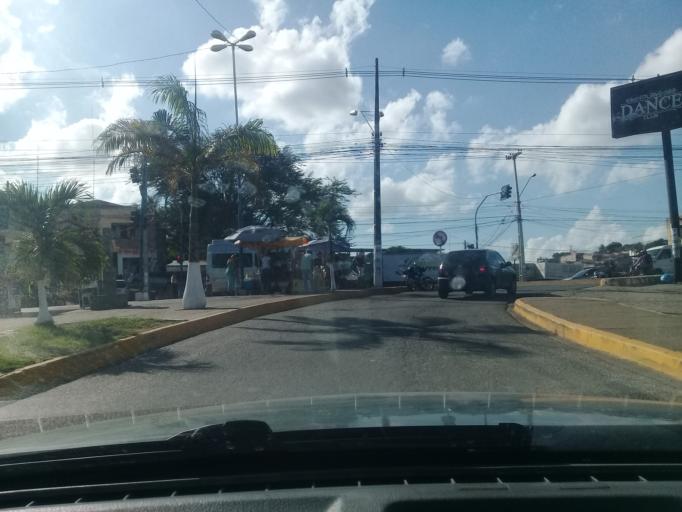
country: BR
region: Pernambuco
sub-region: Vitoria De Santo Antao
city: Vitoria de Santo Antao
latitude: -8.1172
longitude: -35.2969
